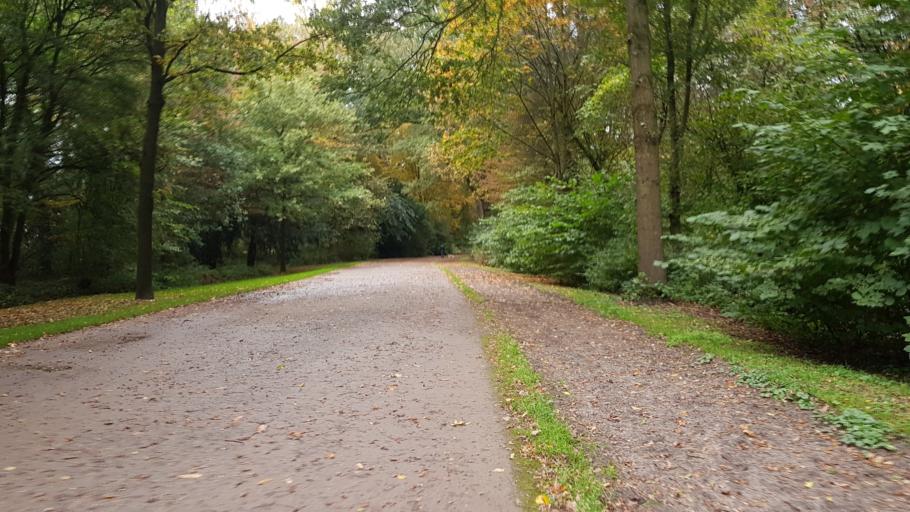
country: DE
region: Bremen
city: Bremen
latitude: 53.0977
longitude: 8.8263
